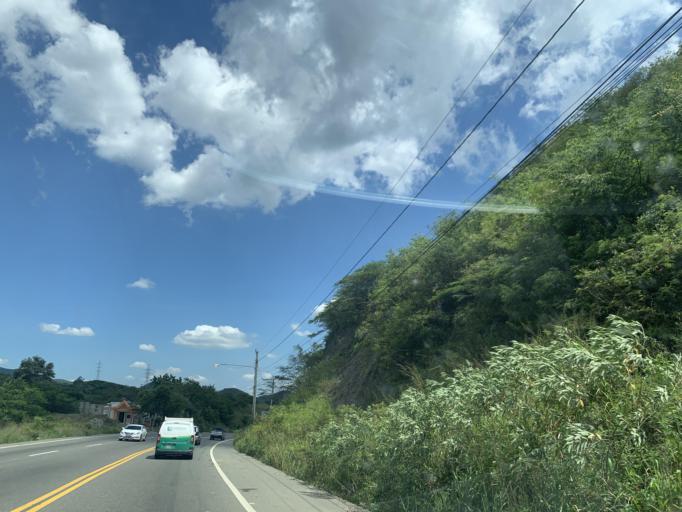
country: DO
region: Santiago
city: Villa Bisono
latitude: 19.6101
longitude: -70.8396
